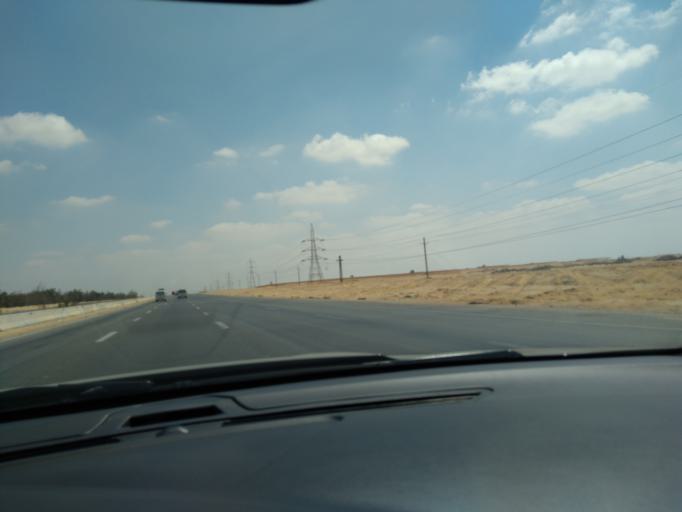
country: EG
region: Al Isma'iliyah
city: At Tall al Kabir
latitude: 30.3939
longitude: 31.9724
